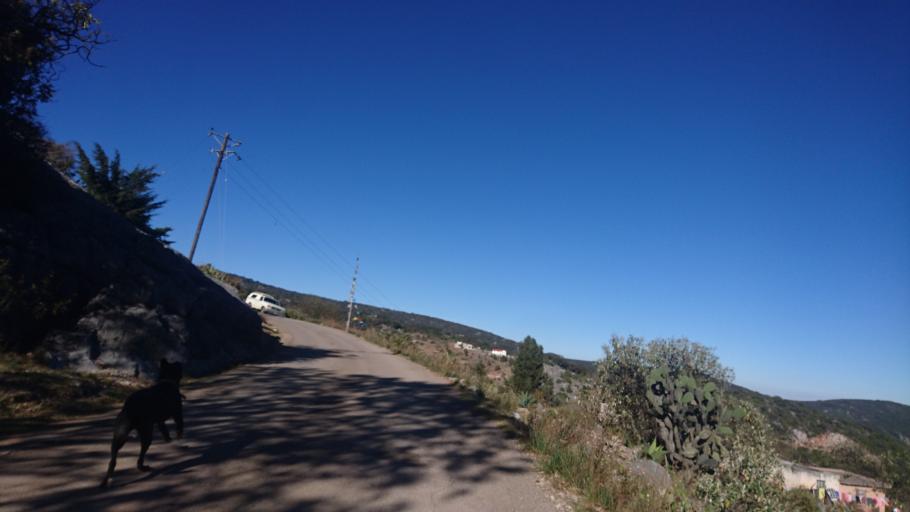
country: MX
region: San Luis Potosi
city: Zaragoza
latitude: 22.0223
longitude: -100.6016
